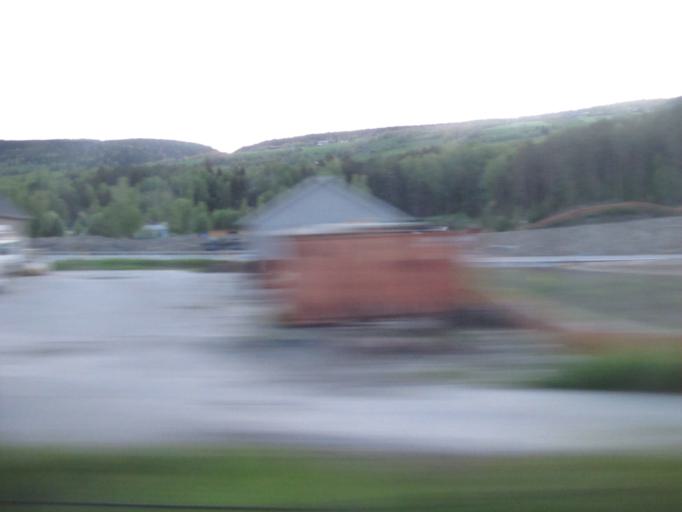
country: NO
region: Oppland
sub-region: Sor-Fron
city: Hundorp
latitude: 61.5651
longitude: 9.9177
